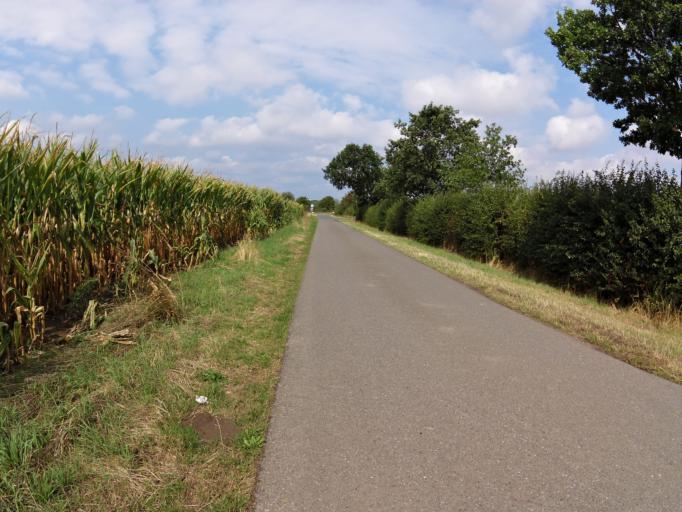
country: DE
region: Lower Saxony
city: Bucken
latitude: 52.7921
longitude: 9.1401
